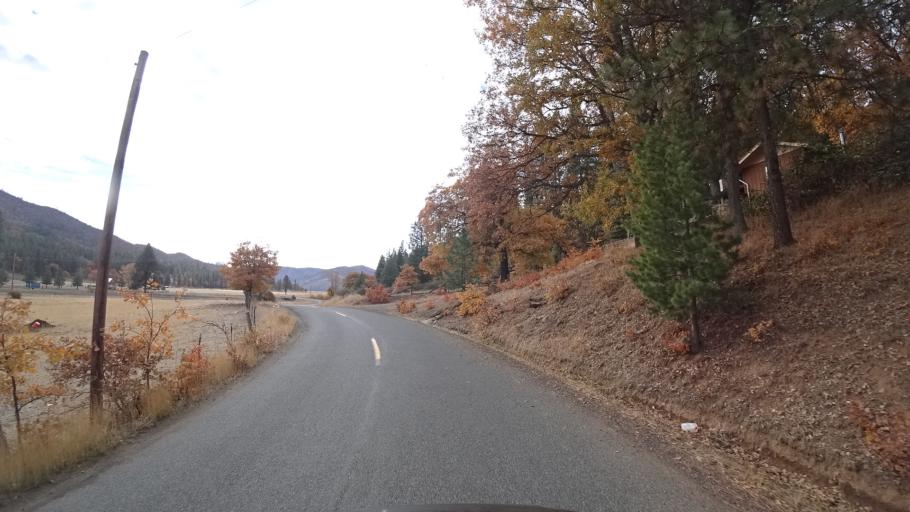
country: US
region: California
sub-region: Siskiyou County
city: Yreka
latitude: 41.6584
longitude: -122.8368
